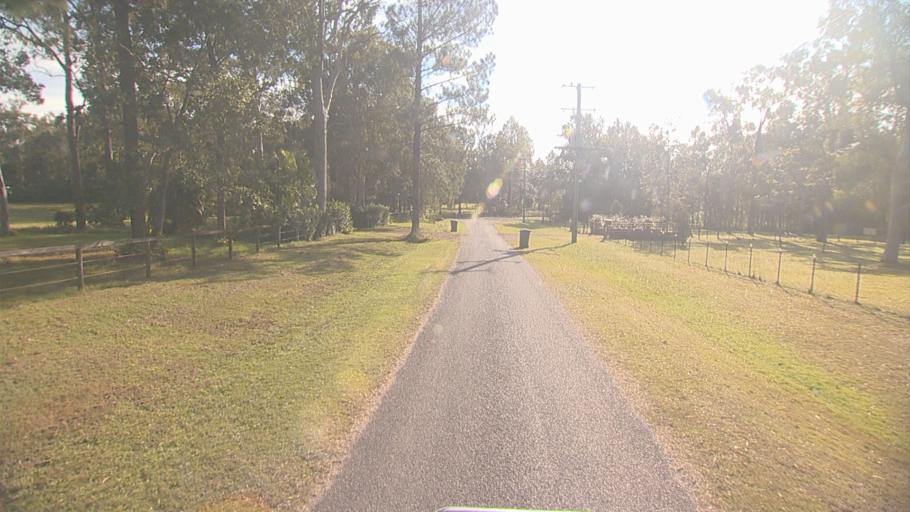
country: AU
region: Queensland
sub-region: Logan
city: Park Ridge South
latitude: -27.7459
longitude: 153.0449
